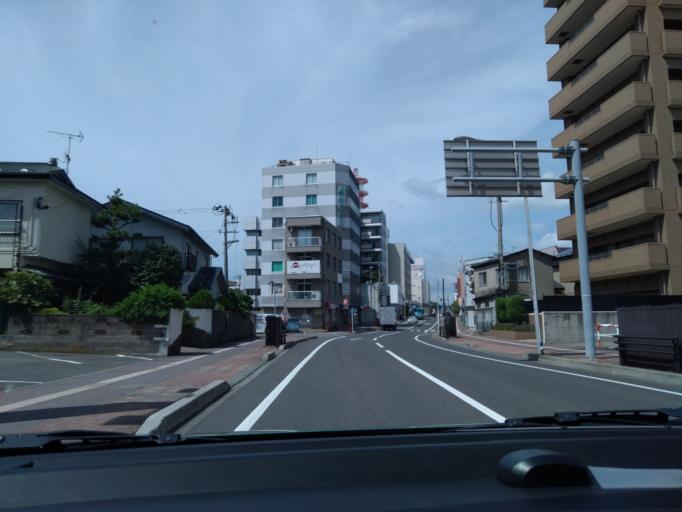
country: JP
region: Akita
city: Akita
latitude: 39.7125
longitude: 140.1249
